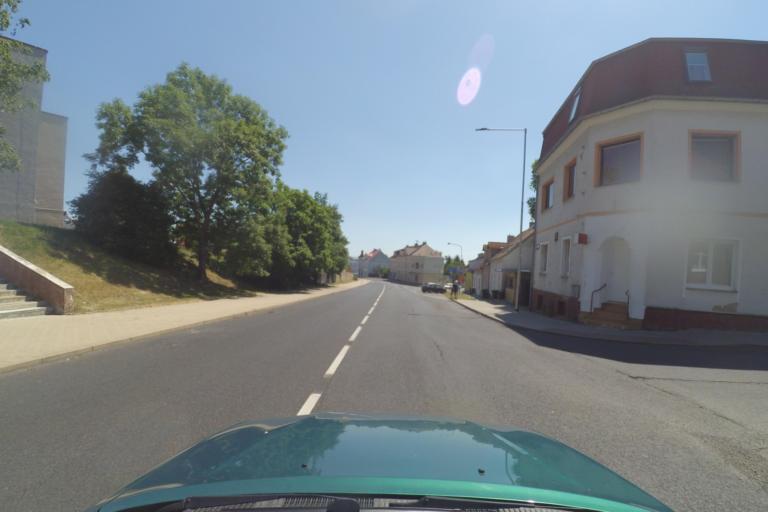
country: CZ
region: Ustecky
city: Krupka
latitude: 50.6813
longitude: 13.8649
